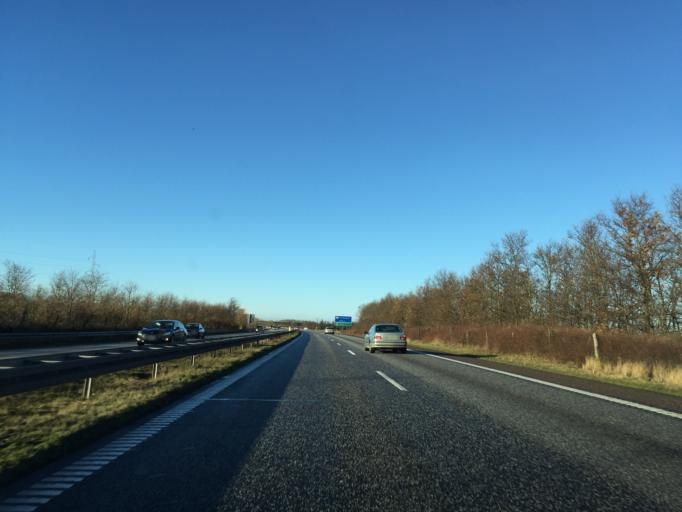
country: DK
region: South Denmark
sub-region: Kerteminde Kommune
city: Langeskov
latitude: 55.3620
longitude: 10.5436
